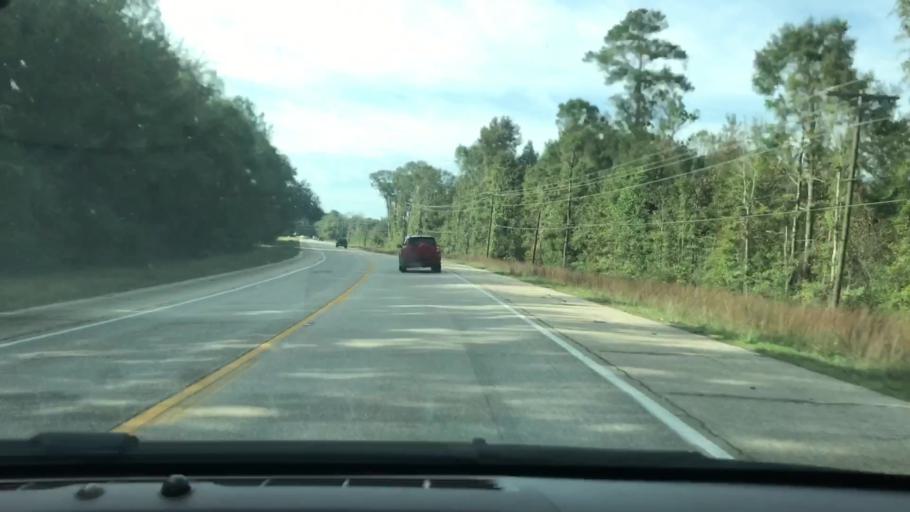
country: US
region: Mississippi
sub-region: Pearl River County
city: Nicholson
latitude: 30.5317
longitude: -89.8624
